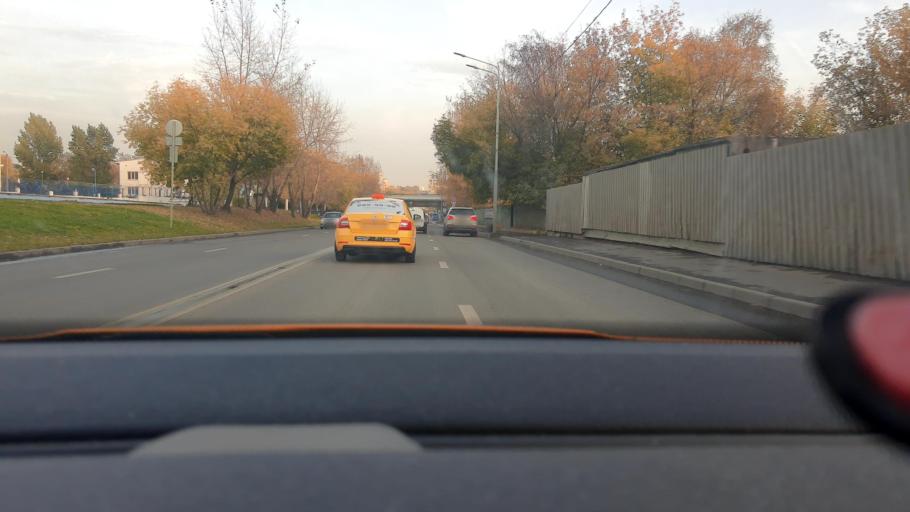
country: RU
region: Moscow
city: Metrogorodok
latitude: 55.8197
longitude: 37.7653
